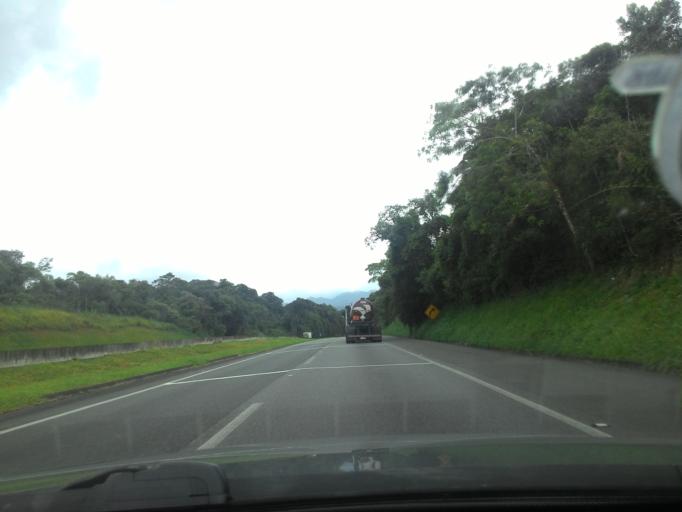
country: BR
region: Sao Paulo
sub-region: Cajati
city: Cajati
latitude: -24.9701
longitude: -48.3973
